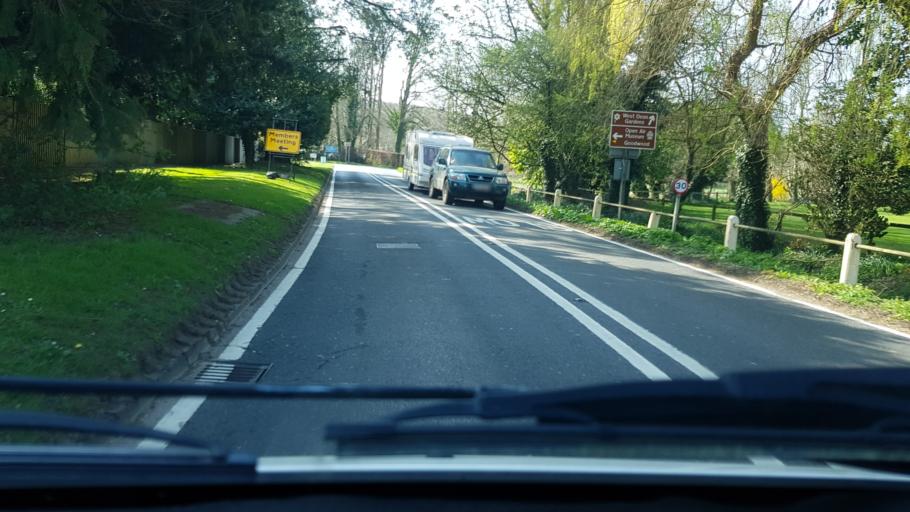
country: GB
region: England
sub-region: West Sussex
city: Boxgrove
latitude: 50.9104
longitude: -0.7556
